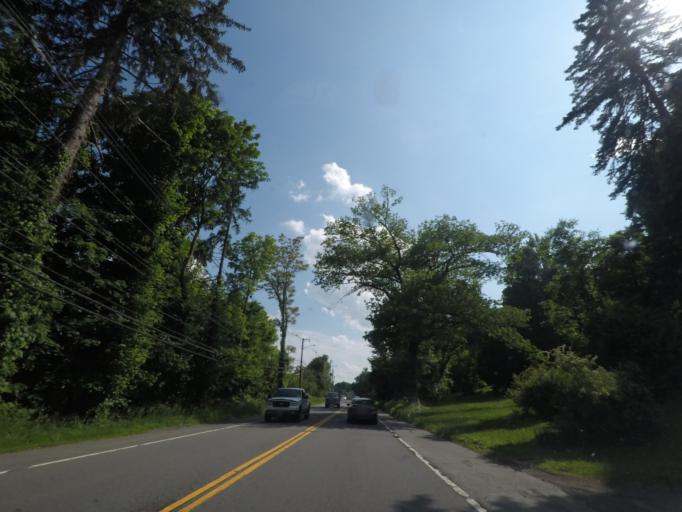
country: US
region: New York
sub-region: Orange County
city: Balmville
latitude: 41.5633
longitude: -74.0016
